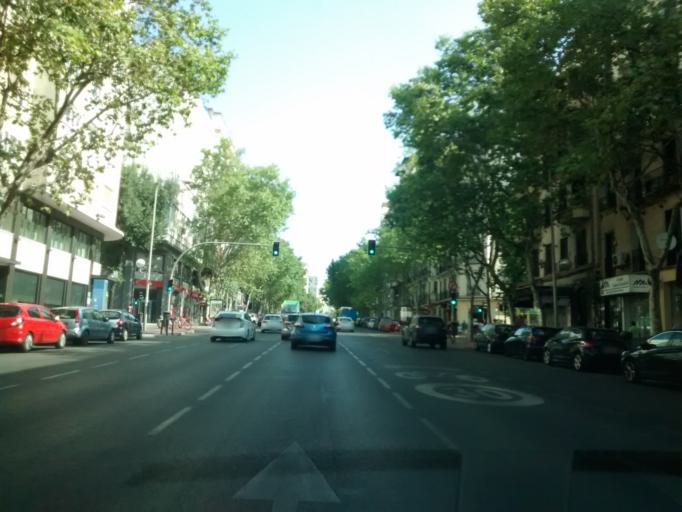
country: ES
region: Madrid
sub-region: Provincia de Madrid
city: Arganzuela
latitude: 40.4048
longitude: -3.6935
